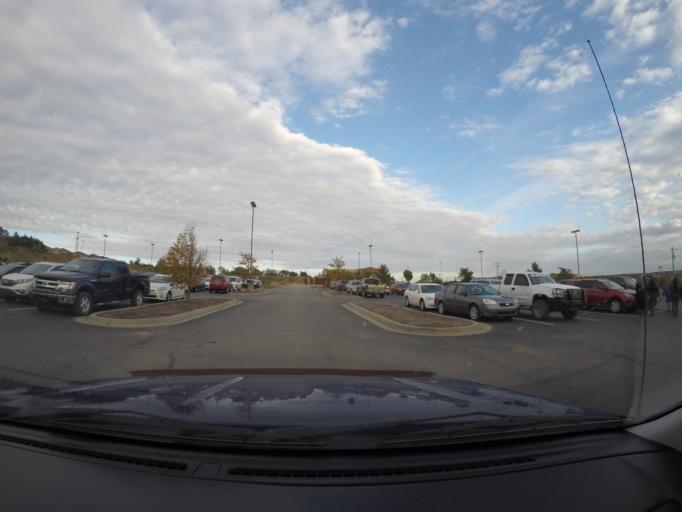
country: US
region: Kansas
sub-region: Shawnee County
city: Topeka
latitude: 39.0586
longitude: -95.7672
